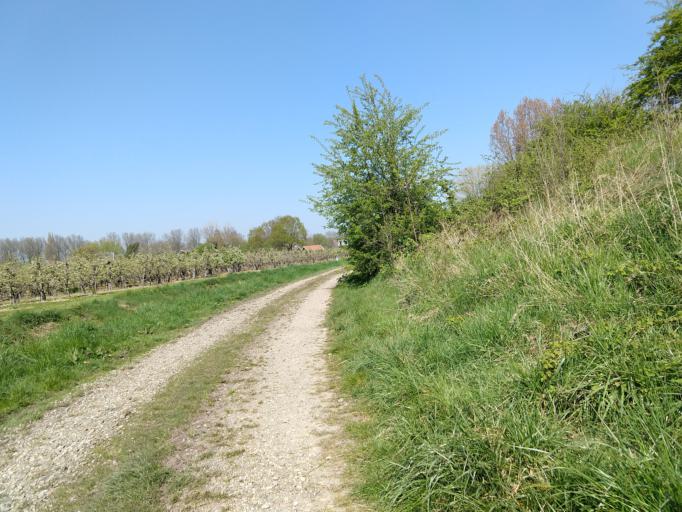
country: NL
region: Zeeland
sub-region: Gemeente Goes
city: Goes
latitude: 51.4893
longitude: 3.8189
